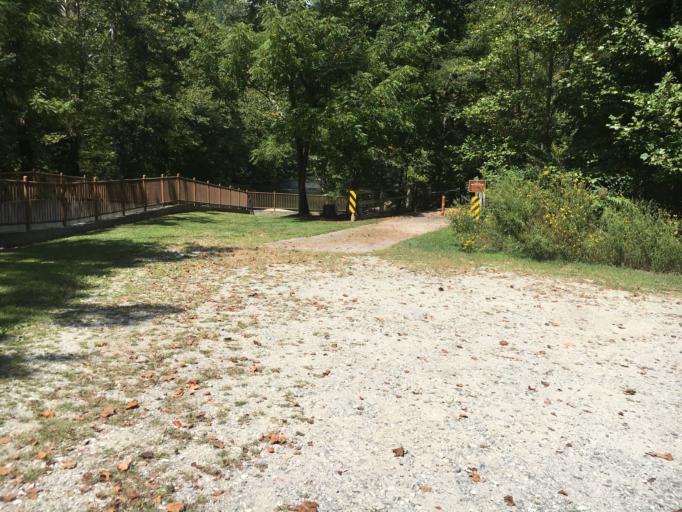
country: US
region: North Carolina
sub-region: Graham County
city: Robbinsville
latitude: 35.2731
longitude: -83.6775
